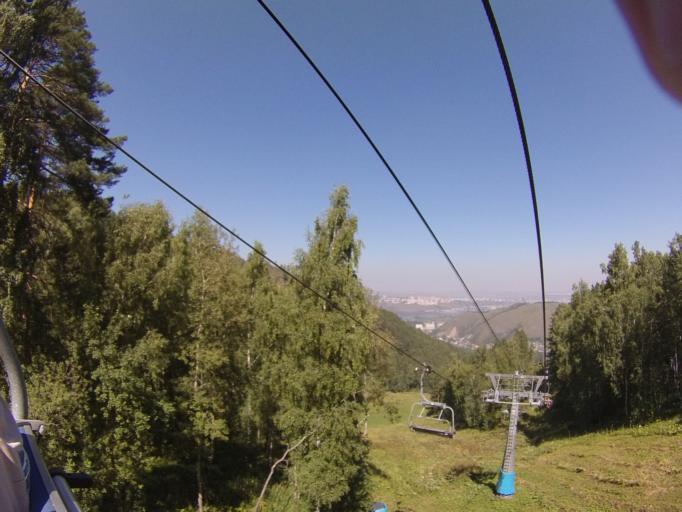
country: RU
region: Krasnoyarskiy
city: Krasnoyarsk
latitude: 55.9512
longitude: 92.7883
